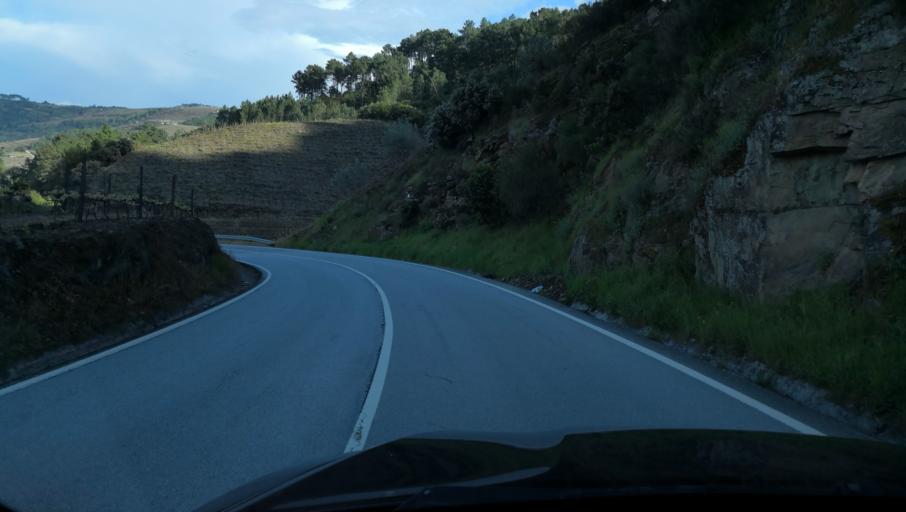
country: PT
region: Vila Real
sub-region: Santa Marta de Penaguiao
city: Santa Marta de Penaguiao
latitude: 41.2200
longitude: -7.7319
